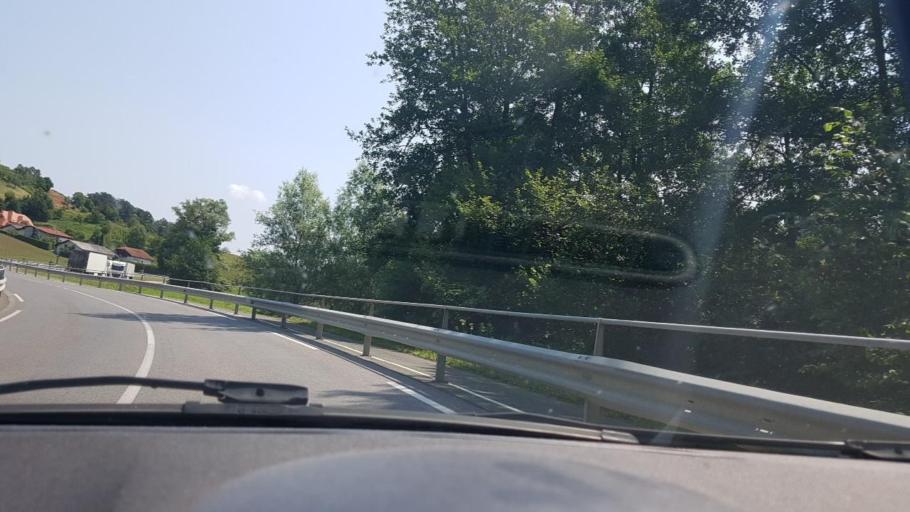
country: SI
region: Rogaska Slatina
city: Rogaska Slatina
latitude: 46.2386
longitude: 15.6085
